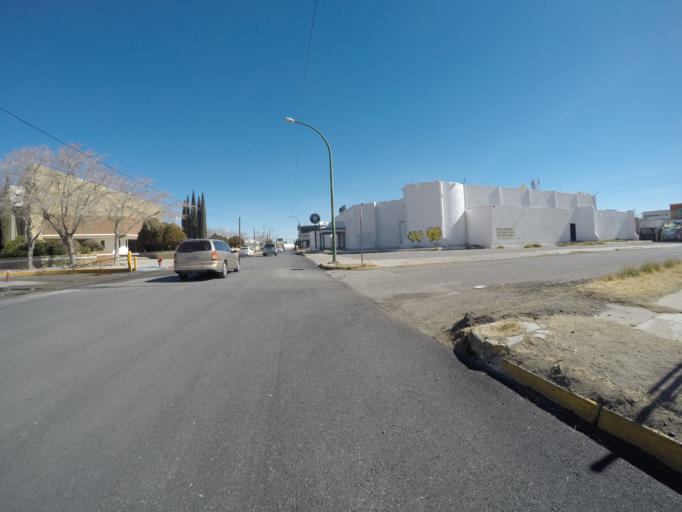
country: MX
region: Chihuahua
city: Ciudad Juarez
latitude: 31.7400
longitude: -106.4569
